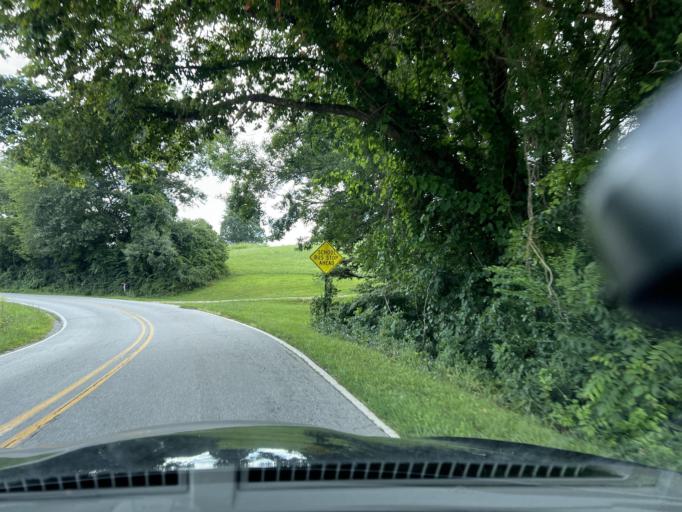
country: US
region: North Carolina
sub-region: Henderson County
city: Hoopers Creek
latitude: 35.4393
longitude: -82.4523
